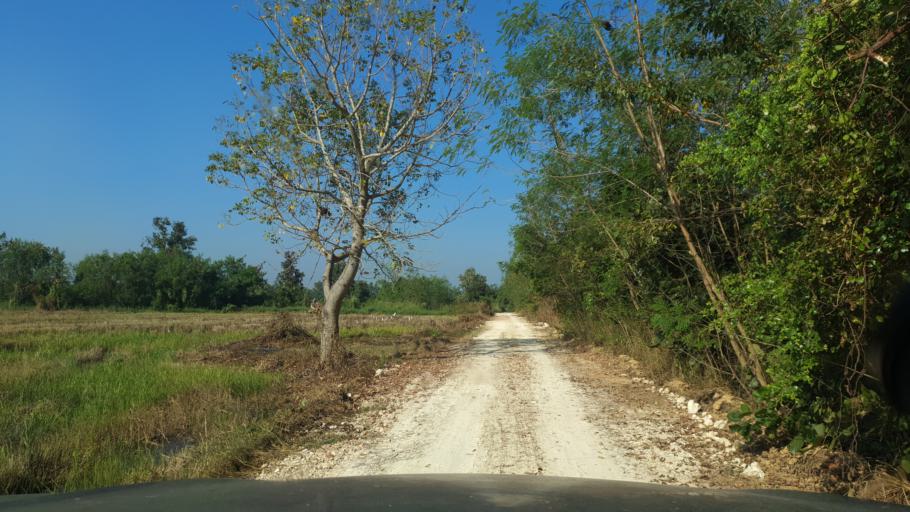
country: TH
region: Chiang Mai
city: Saraphi
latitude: 18.7097
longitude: 99.0817
